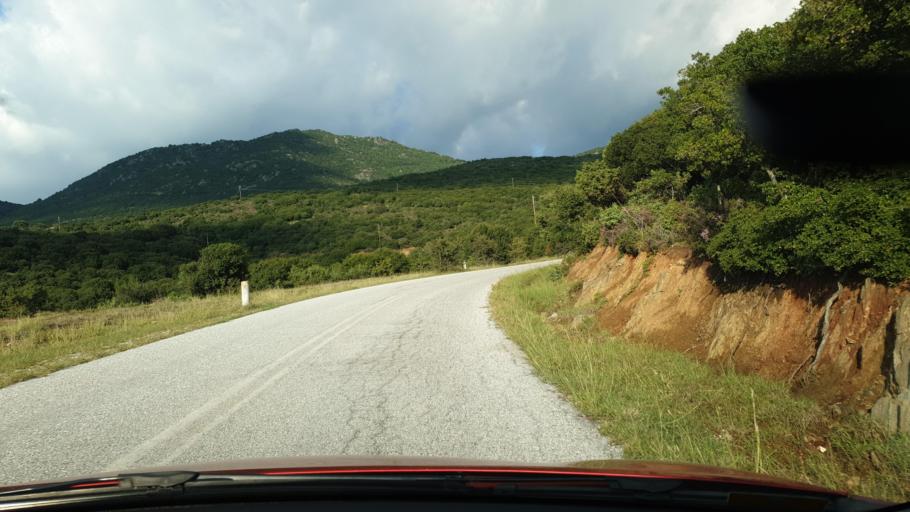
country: GR
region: Central Macedonia
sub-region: Nomos Thessalonikis
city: Peristera
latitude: 40.5216
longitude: 23.1862
